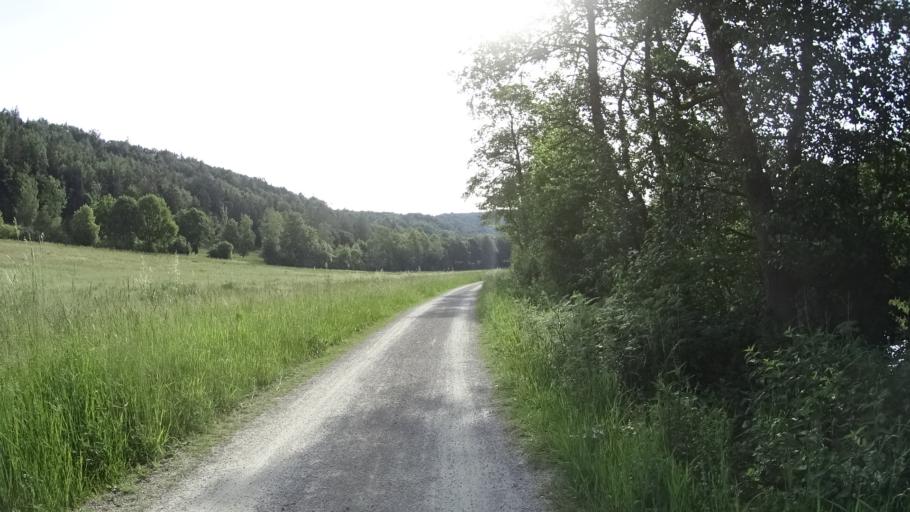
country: DE
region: Bavaria
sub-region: Lower Bavaria
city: Essing
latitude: 48.9408
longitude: 11.7625
